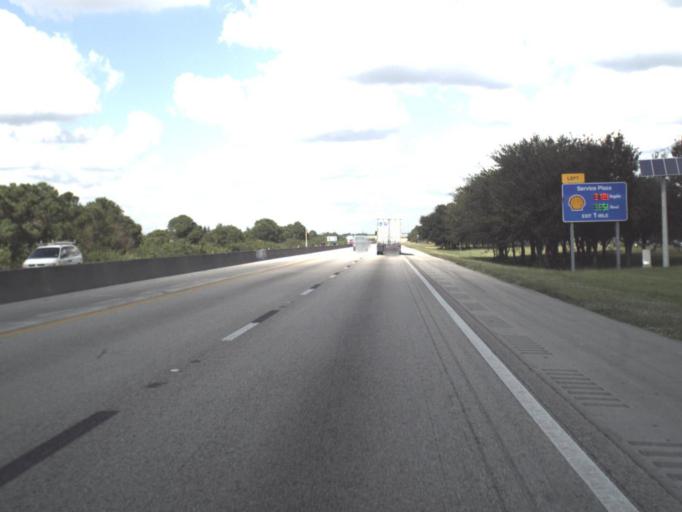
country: US
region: Florida
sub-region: Saint Lucie County
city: Port Saint Lucie
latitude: 27.2858
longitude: -80.3653
